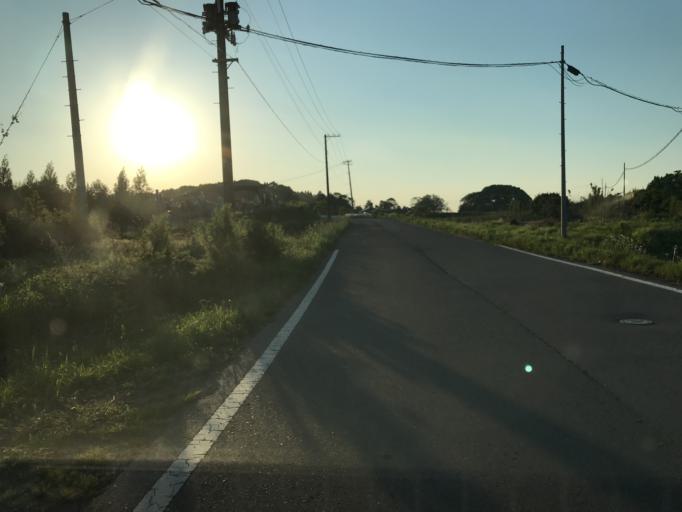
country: JP
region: Fukushima
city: Sukagawa
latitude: 37.1794
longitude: 140.3340
